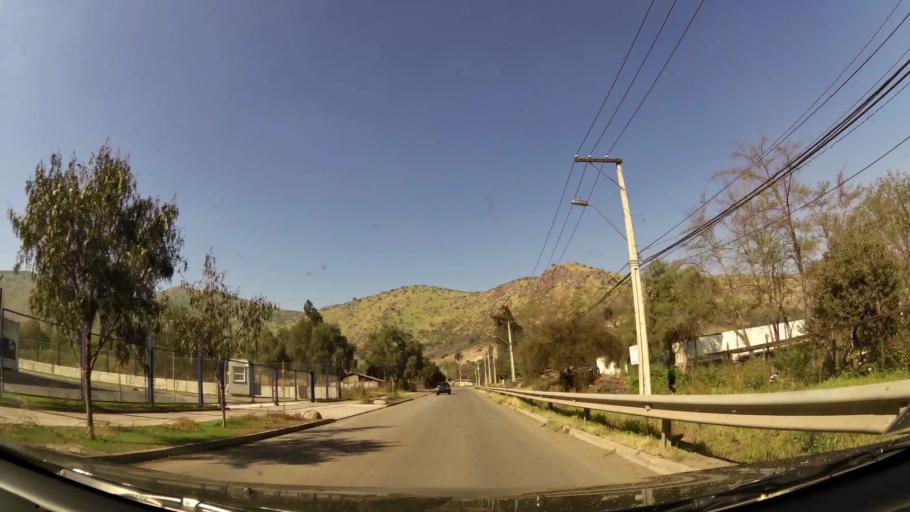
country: CL
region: Santiago Metropolitan
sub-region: Provincia de Chacabuco
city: Chicureo Abajo
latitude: -33.3416
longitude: -70.6980
